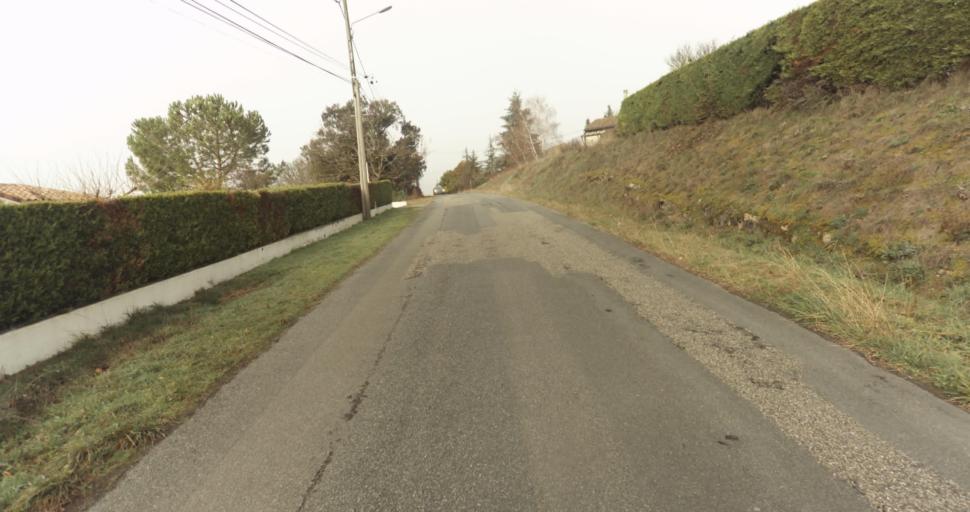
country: FR
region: Midi-Pyrenees
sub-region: Departement du Lot
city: Figeac
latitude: 44.6193
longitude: 2.0246
